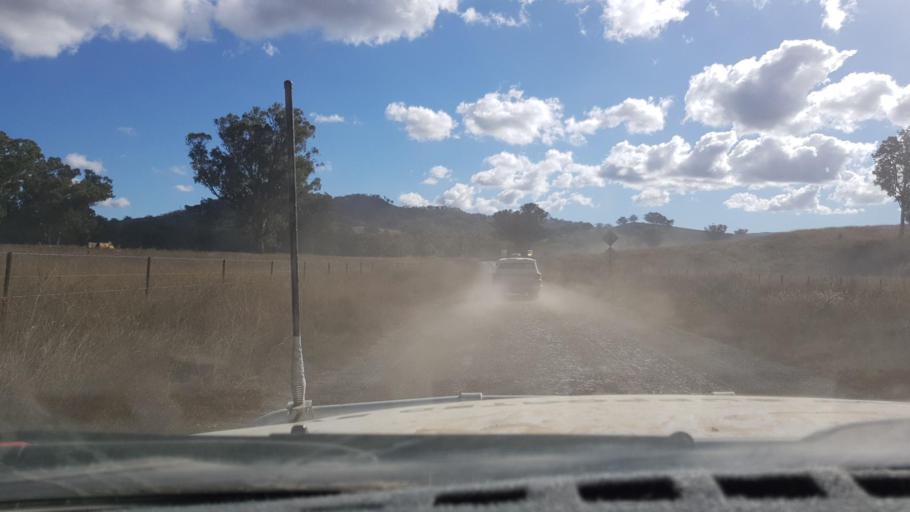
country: AU
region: New South Wales
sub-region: Tamworth Municipality
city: Manilla
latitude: -30.6184
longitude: 150.5147
